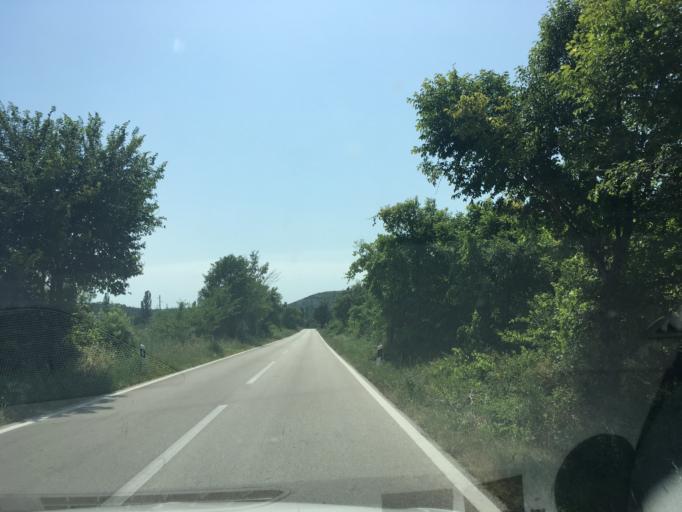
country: HR
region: Sibensko-Kniniska
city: Zaton
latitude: 43.9317
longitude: 15.8267
